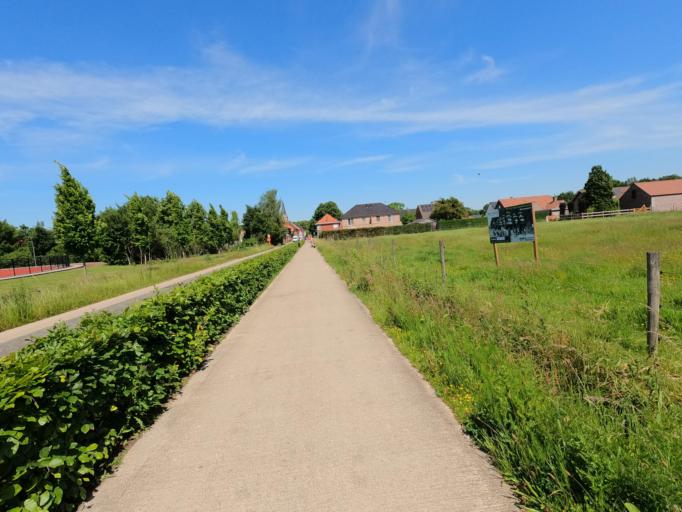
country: BE
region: Flanders
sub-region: Provincie Antwerpen
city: Kalmthout
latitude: 51.3794
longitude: 4.4802
